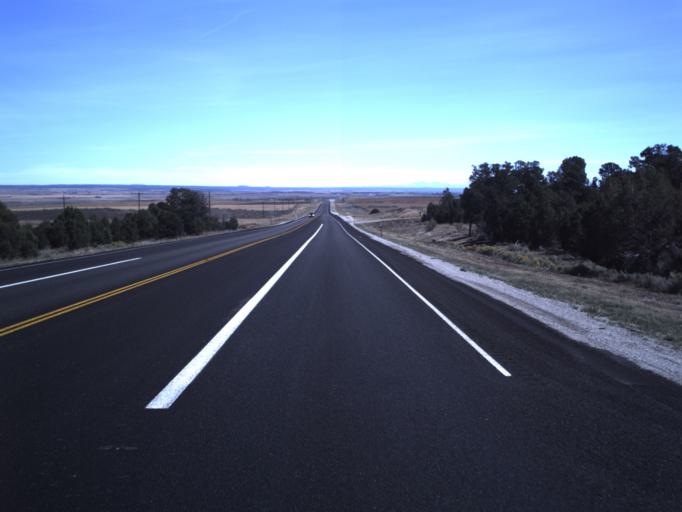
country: US
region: Colorado
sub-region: Dolores County
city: Dove Creek
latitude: 37.8225
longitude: -109.0631
